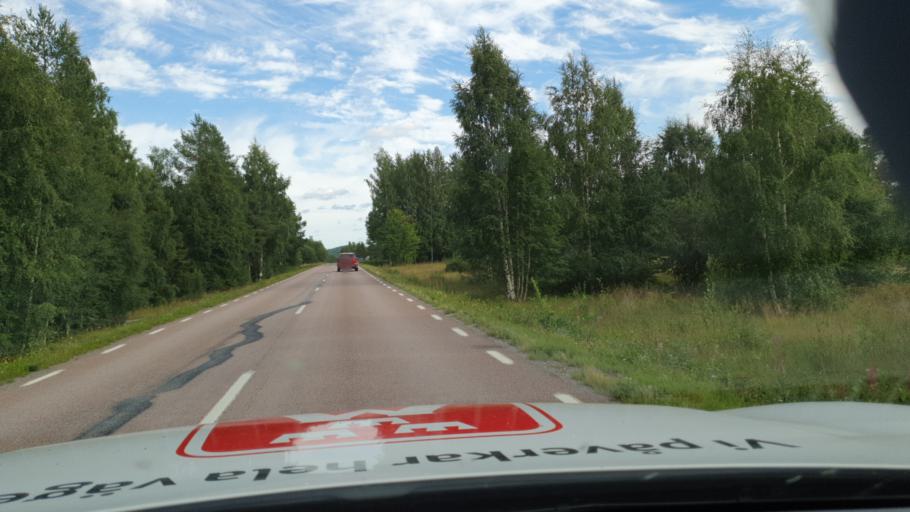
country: SE
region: Jaemtland
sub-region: Stroemsunds Kommun
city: Stroemsund
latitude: 63.6467
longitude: 16.0063
